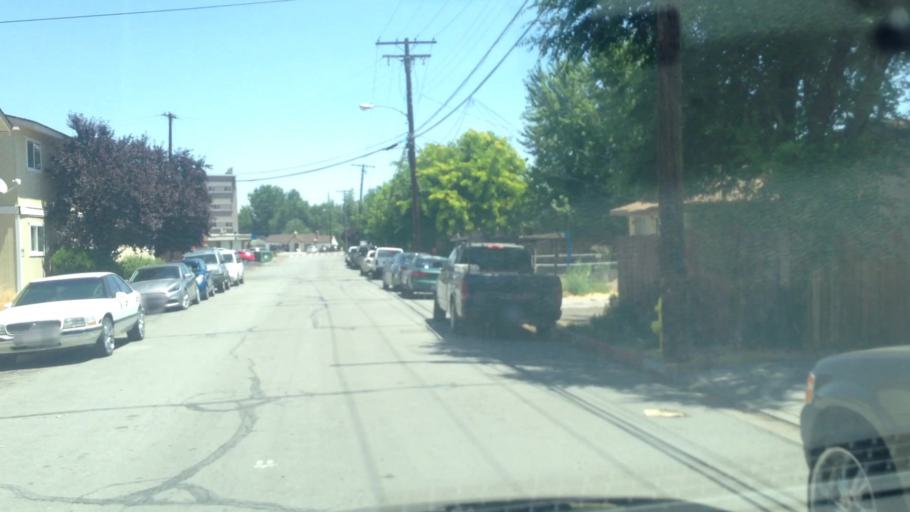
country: US
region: Nevada
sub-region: Washoe County
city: Sparks
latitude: 39.5429
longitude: -119.7550
